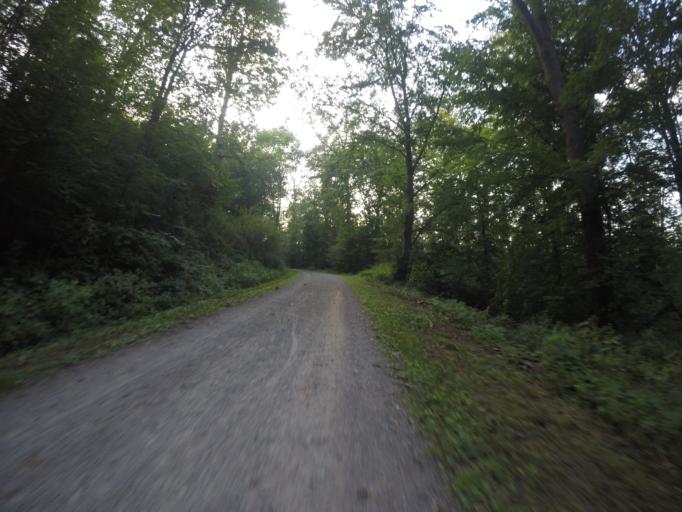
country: DE
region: Baden-Wuerttemberg
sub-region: Regierungsbezirk Stuttgart
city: Stuttgart
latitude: 48.7560
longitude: 9.1204
